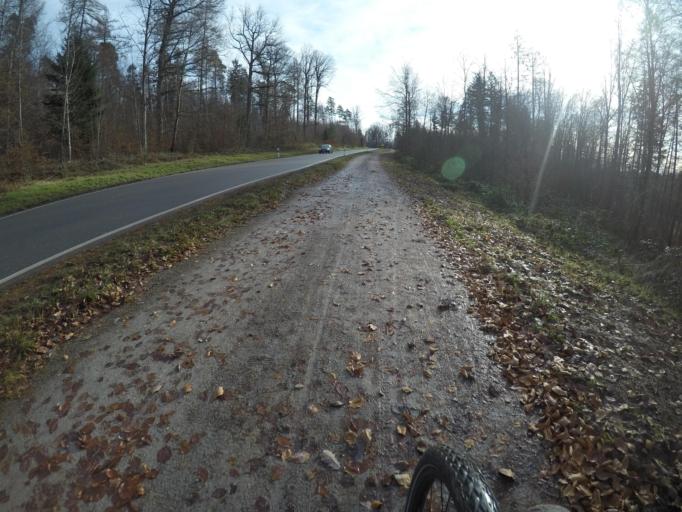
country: DE
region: Baden-Wuerttemberg
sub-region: Regierungsbezirk Stuttgart
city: Winterbach
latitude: 48.7628
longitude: 9.4887
